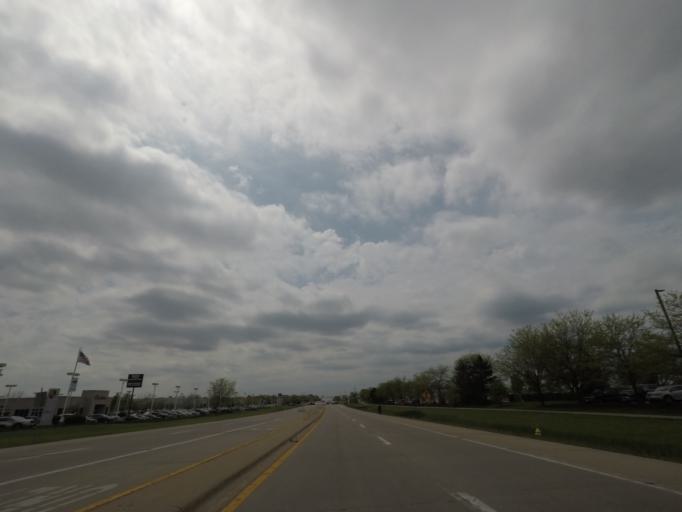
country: US
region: Illinois
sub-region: Winnebago County
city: Cherry Valley
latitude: 42.2747
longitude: -88.9801
